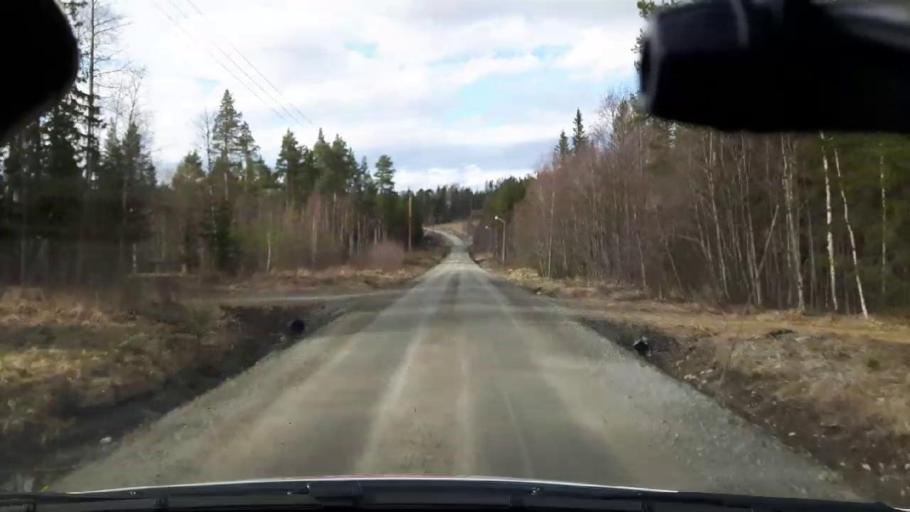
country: SE
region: Jaemtland
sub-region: Bergs Kommun
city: Hoverberg
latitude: 62.8776
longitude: 14.6666
